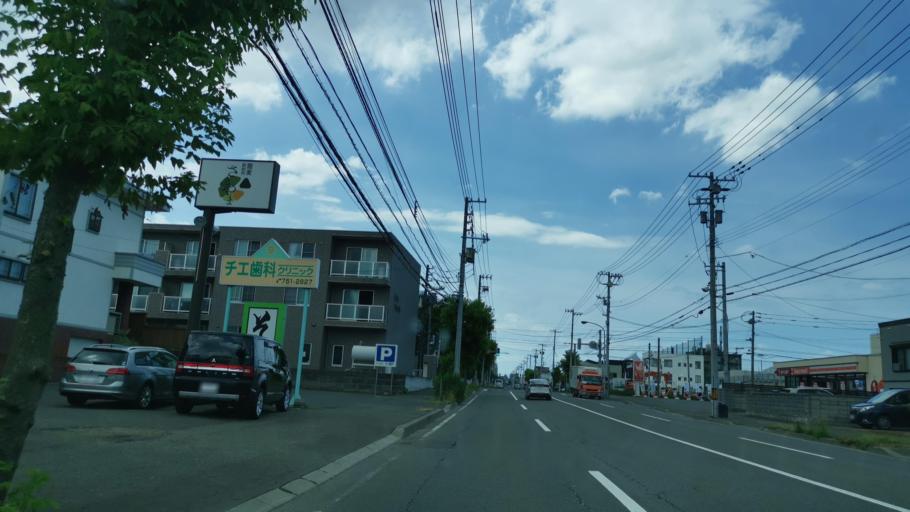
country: JP
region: Hokkaido
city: Sapporo
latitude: 43.0741
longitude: 141.3940
